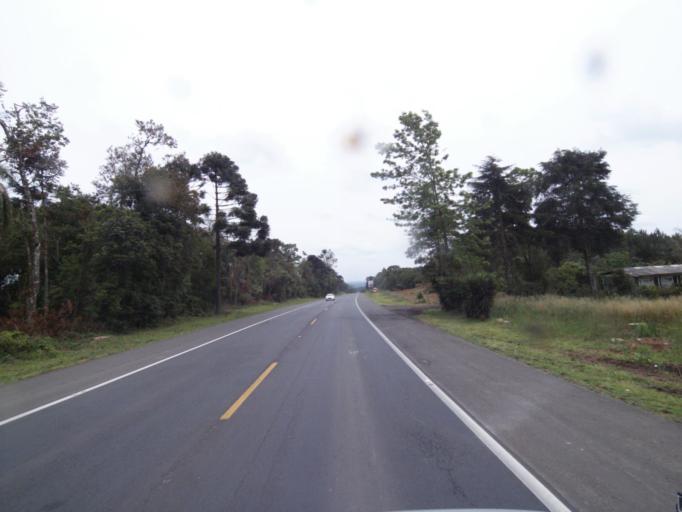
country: BR
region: Parana
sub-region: Irati
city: Irati
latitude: -25.4717
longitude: -50.4954
